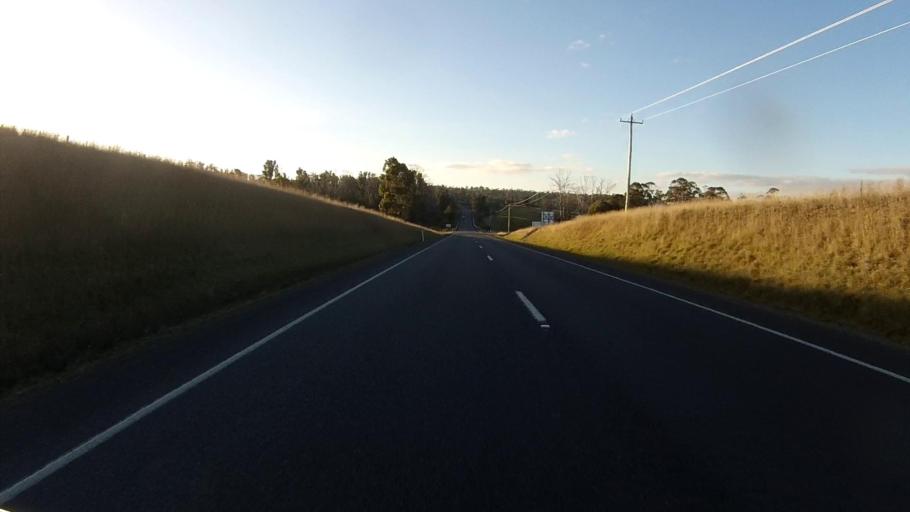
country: AU
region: Tasmania
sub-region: Sorell
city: Sorell
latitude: -42.8651
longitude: 147.8225
